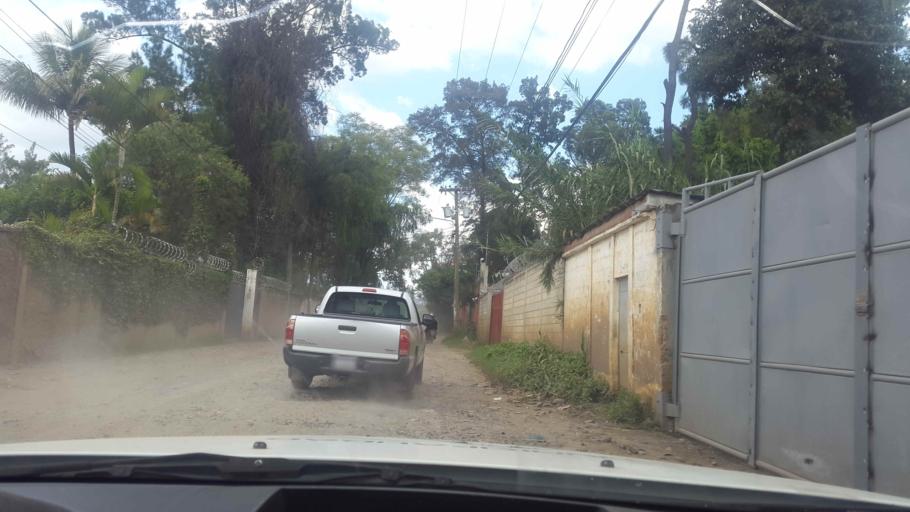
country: GT
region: Guatemala
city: Petapa
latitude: 14.5171
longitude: -90.5369
